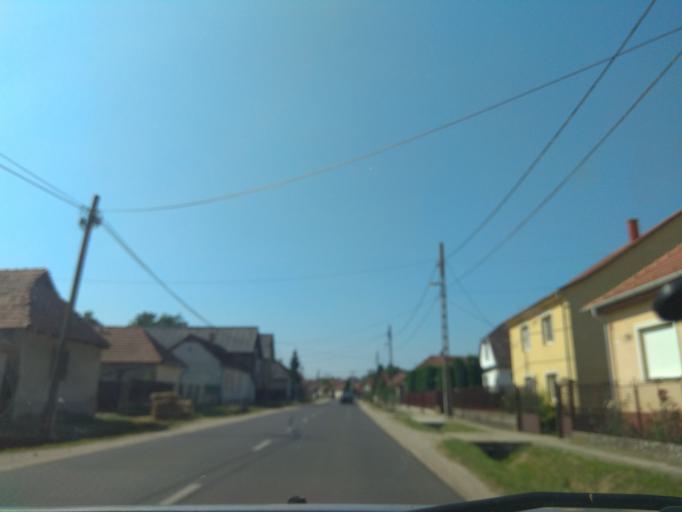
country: HU
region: Borsod-Abauj-Zemplen
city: Harsany
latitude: 47.9714
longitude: 20.7412
